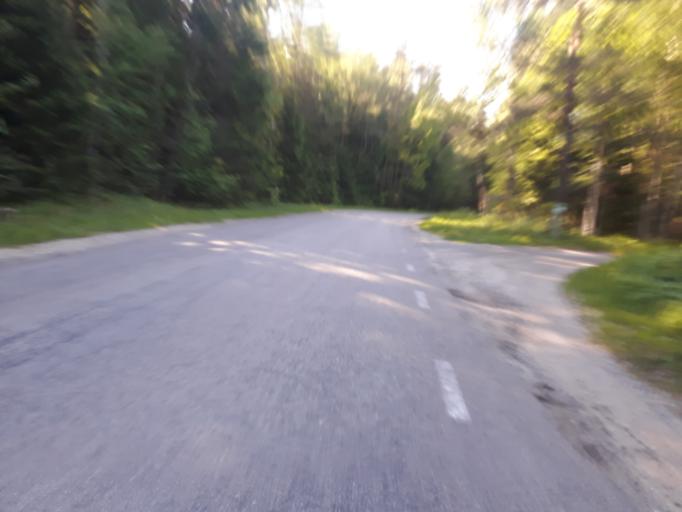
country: EE
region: Harju
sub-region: Loksa linn
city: Loksa
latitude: 59.5668
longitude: 25.9727
